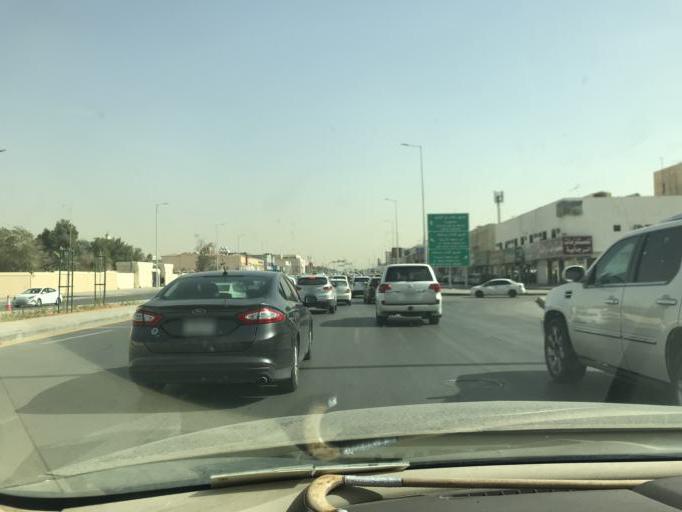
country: SA
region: Ar Riyad
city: Riyadh
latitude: 24.7886
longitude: 46.7460
